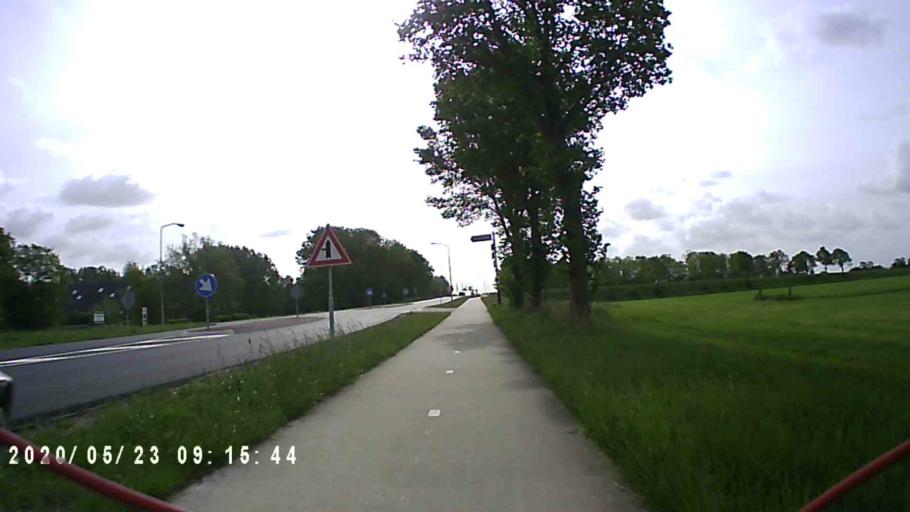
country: NL
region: Groningen
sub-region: Gemeente Bedum
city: Bedum
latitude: 53.3022
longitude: 6.6461
